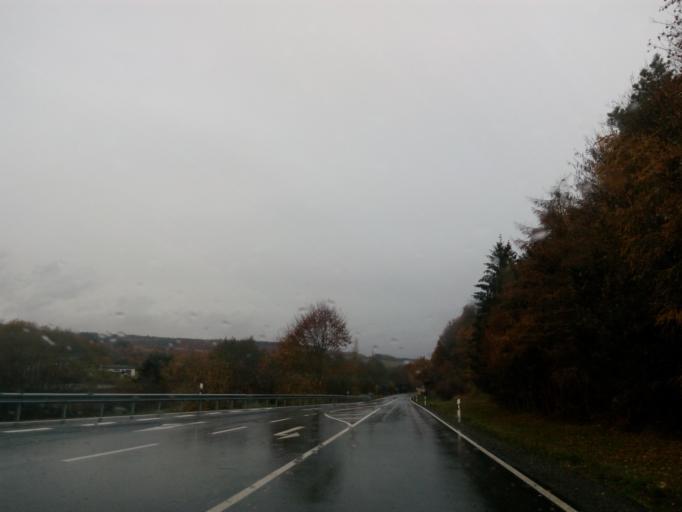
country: DE
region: Rheinland-Pfalz
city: Oberreidenbach
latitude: 49.7118
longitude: 7.4552
